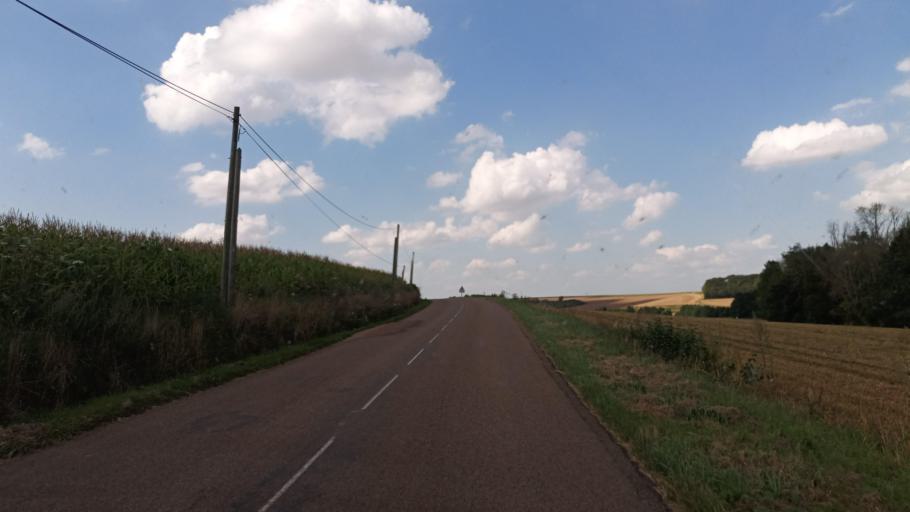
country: FR
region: Bourgogne
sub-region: Departement de l'Yonne
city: Saint-Valerien
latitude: 48.2228
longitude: 3.0657
